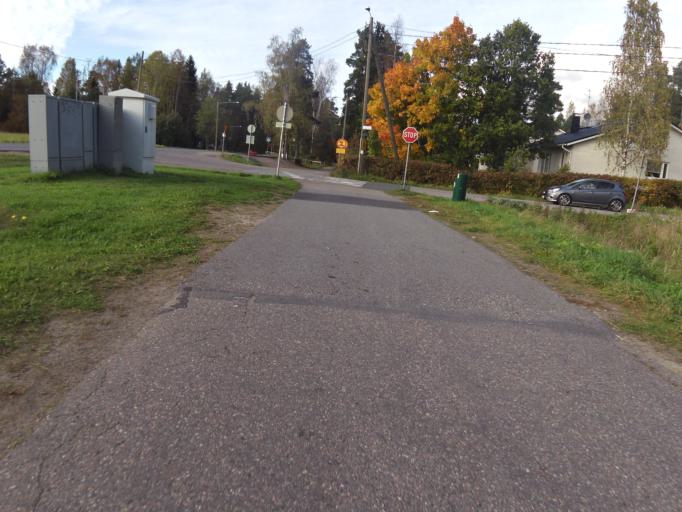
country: FI
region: Uusimaa
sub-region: Helsinki
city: Kilo
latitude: 60.2784
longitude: 24.7500
